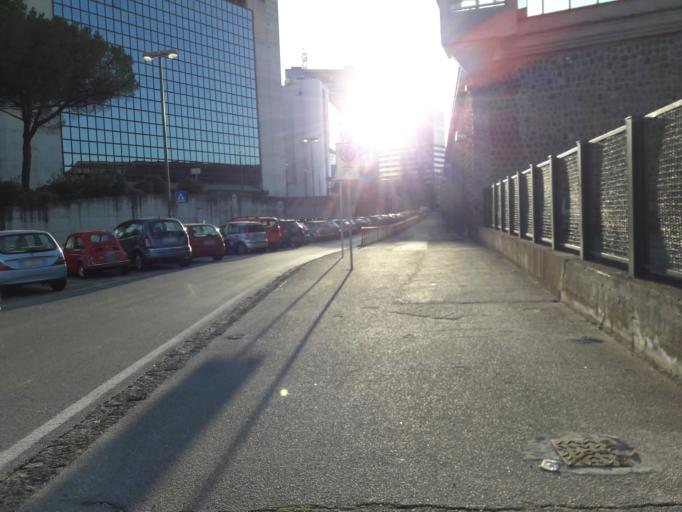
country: IT
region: Campania
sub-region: Provincia di Napoli
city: Napoli
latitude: 40.8598
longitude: 14.2812
